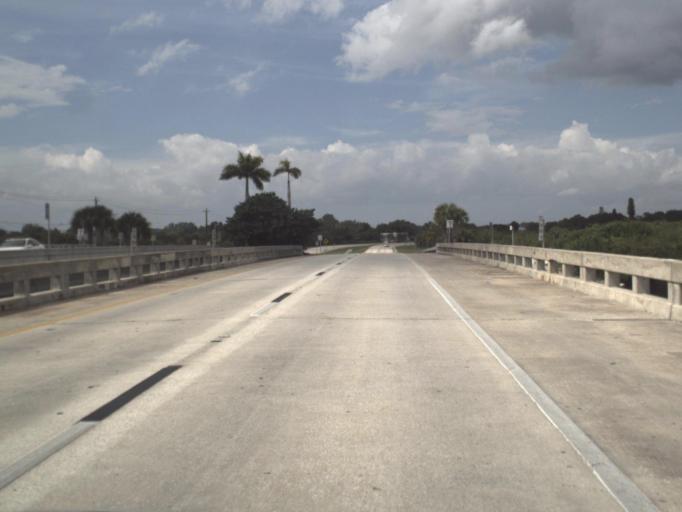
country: US
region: Florida
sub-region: Manatee County
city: Memphis
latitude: 27.5679
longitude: -82.5683
